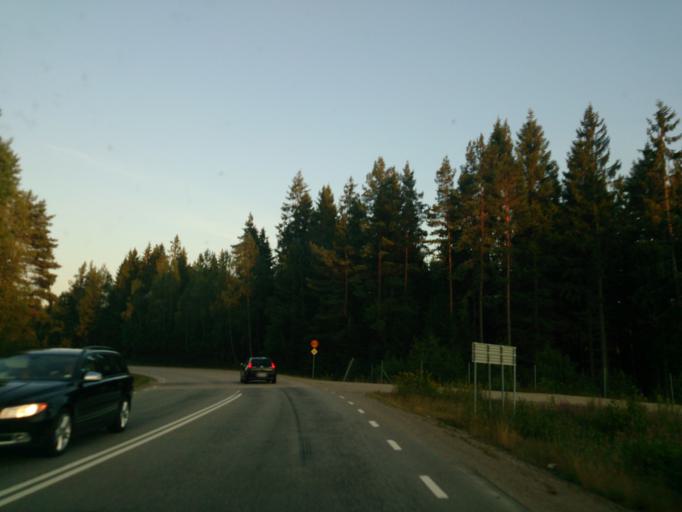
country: SE
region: Kronoberg
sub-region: Alvesta Kommun
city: Alvesta
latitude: 56.9144
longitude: 14.5009
